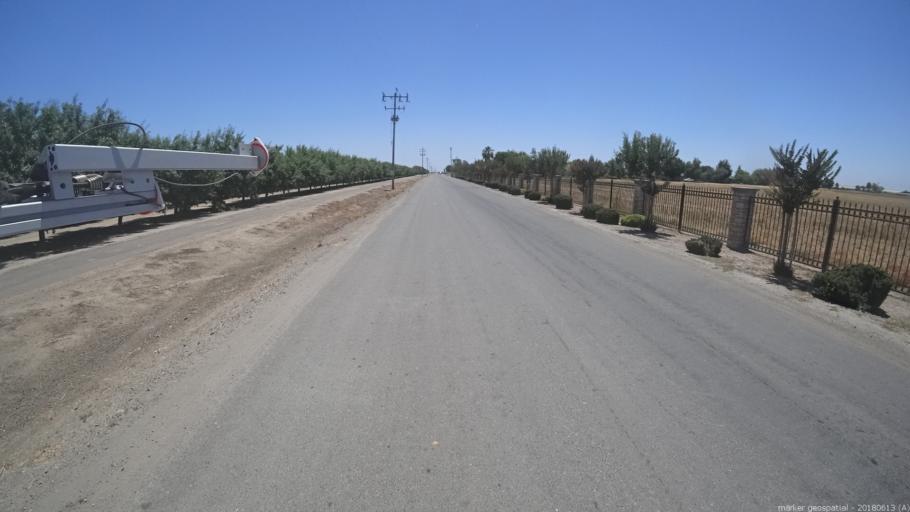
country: US
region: California
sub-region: Madera County
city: Fairmead
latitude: 36.9963
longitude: -120.2742
